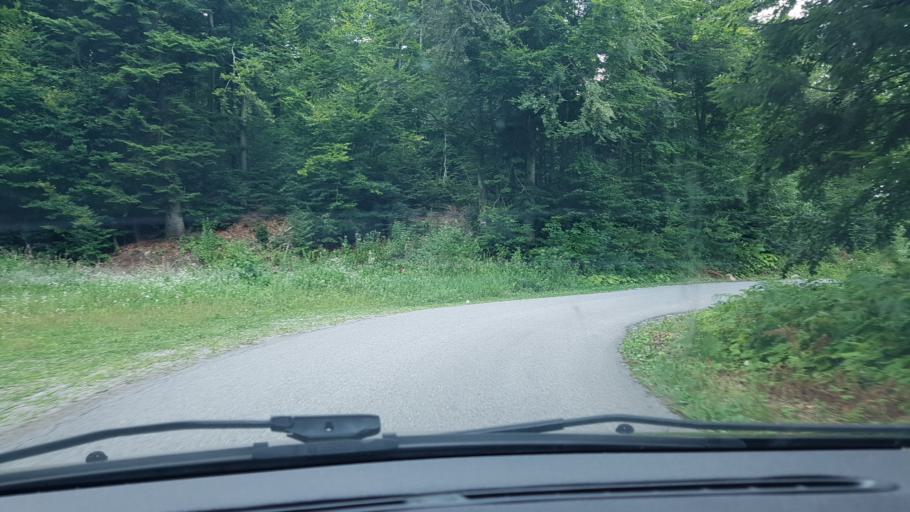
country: HR
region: Primorsko-Goranska
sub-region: Grad Delnice
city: Delnice
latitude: 45.3769
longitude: 14.7048
